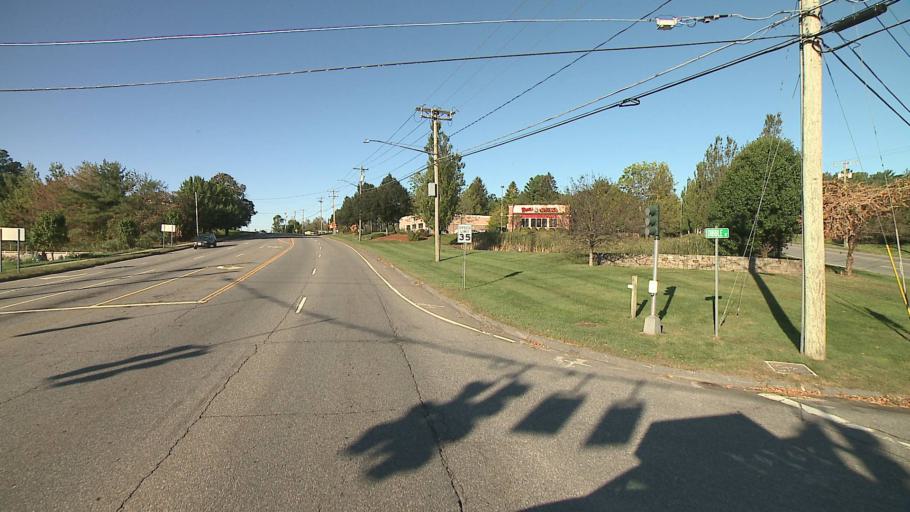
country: US
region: Connecticut
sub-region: Litchfield County
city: Torrington
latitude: 41.8209
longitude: -73.0842
